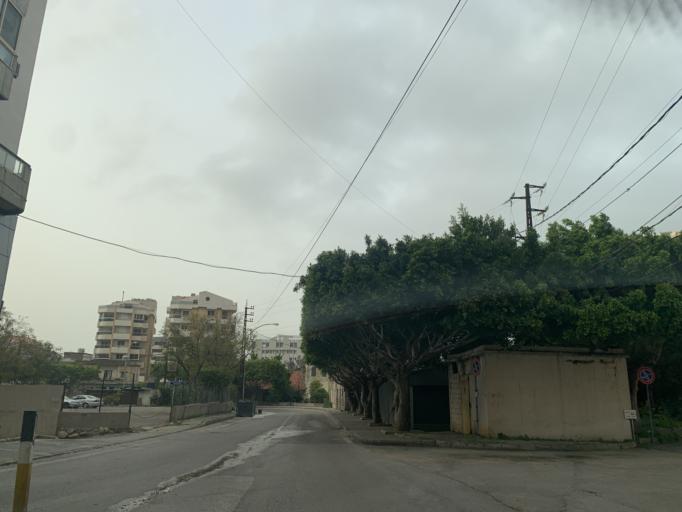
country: LB
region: Mont-Liban
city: Djounie
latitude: 33.9795
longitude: 35.6287
